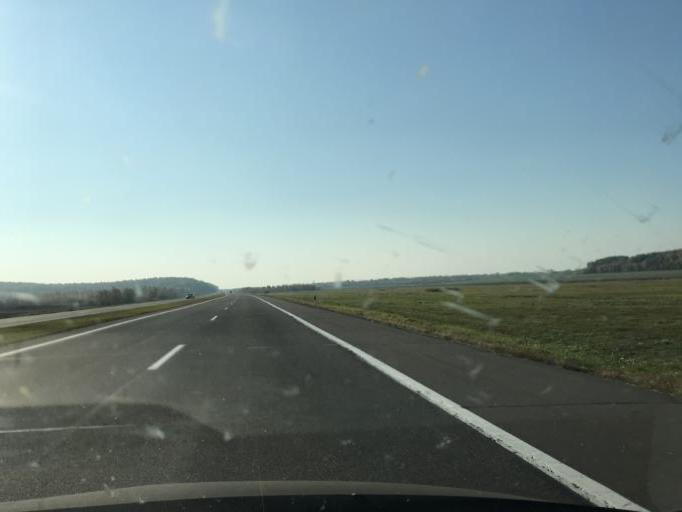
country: BY
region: Minsk
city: Snow
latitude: 53.2531
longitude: 26.2276
